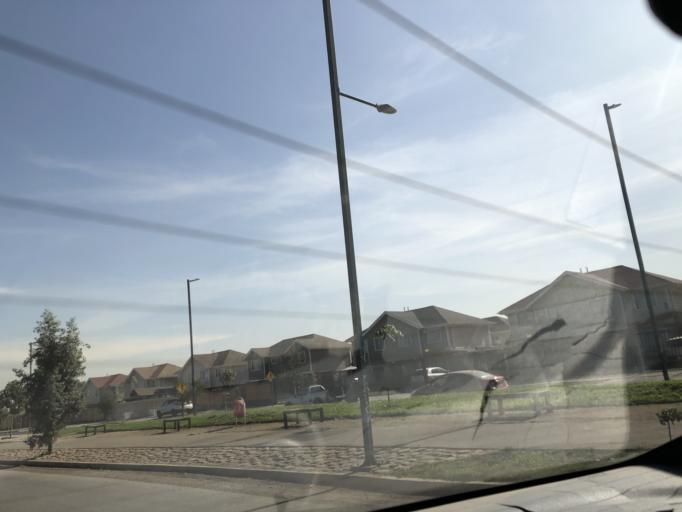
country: CL
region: Santiago Metropolitan
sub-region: Provincia de Cordillera
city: Puente Alto
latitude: -33.5972
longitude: -70.5984
